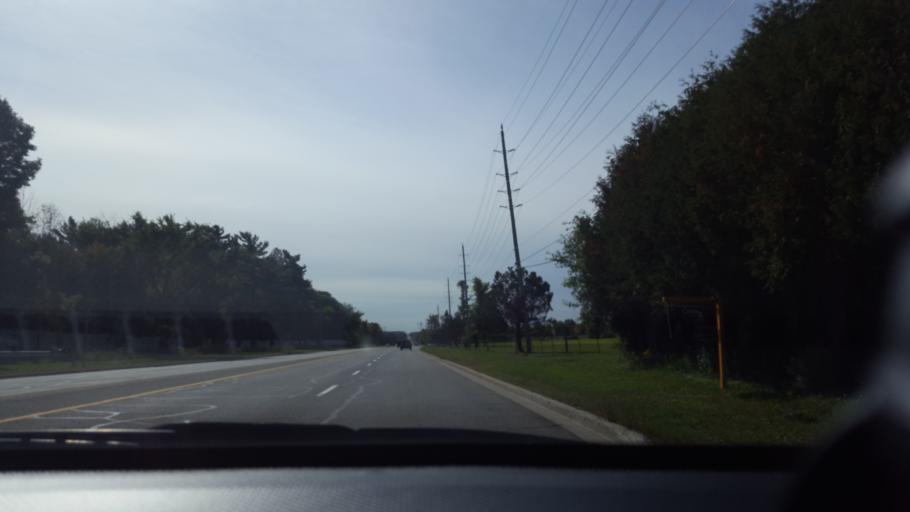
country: CA
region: Ontario
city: Newmarket
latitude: 44.0055
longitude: -79.4969
